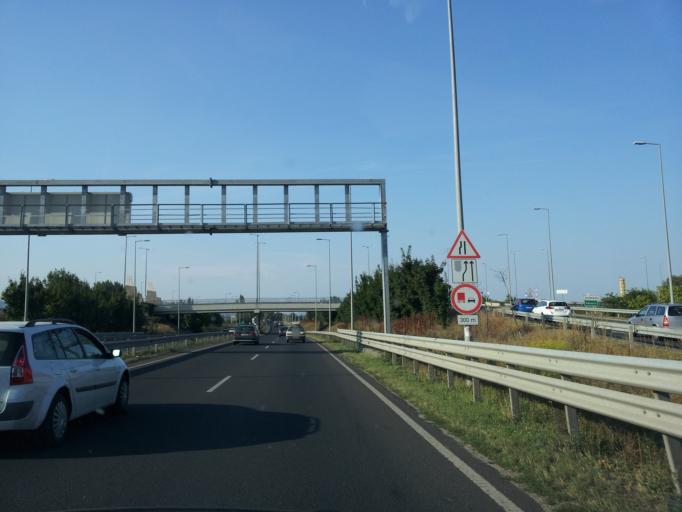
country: HU
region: Pest
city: Budakalasz
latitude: 47.6186
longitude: 19.0663
